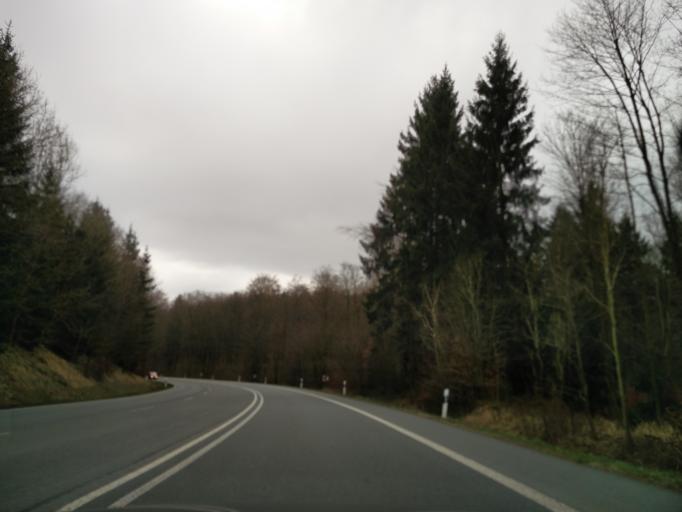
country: DE
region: North Rhine-Westphalia
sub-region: Regierungsbezirk Detmold
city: Willebadessen
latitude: 51.5646
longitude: 9.0026
